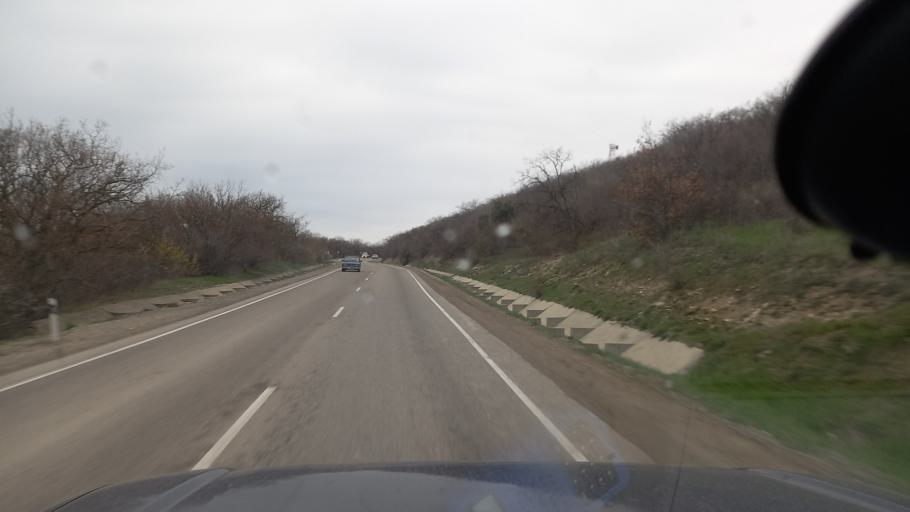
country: RU
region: Krasnodarskiy
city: Sukko
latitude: 44.8394
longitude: 37.4196
